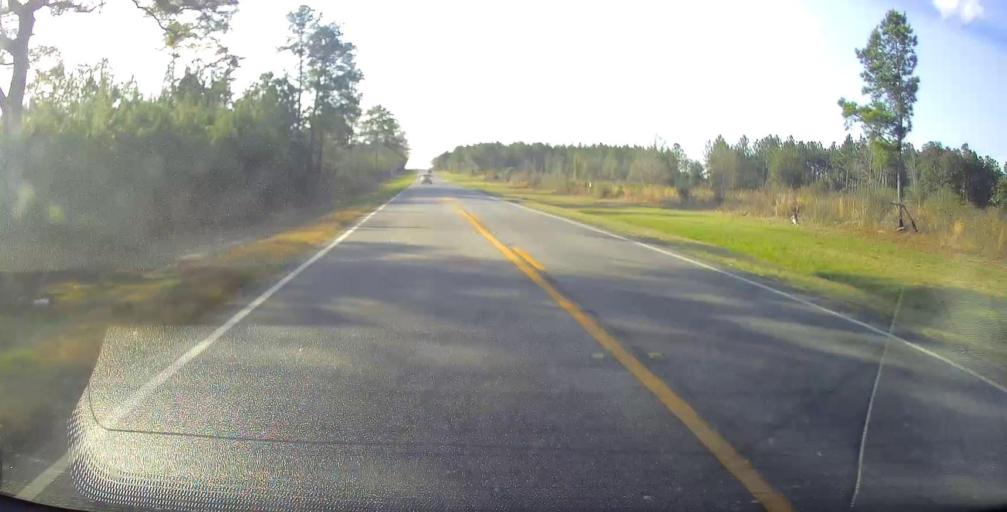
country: US
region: Georgia
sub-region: Tattnall County
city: Reidsville
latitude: 32.1242
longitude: -82.2040
